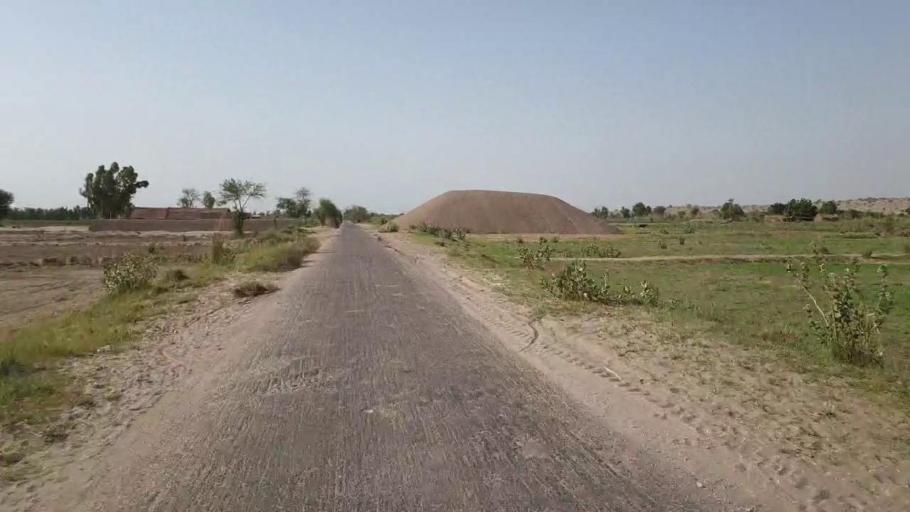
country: PK
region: Sindh
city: Kandiari
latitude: 26.7003
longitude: 68.9645
